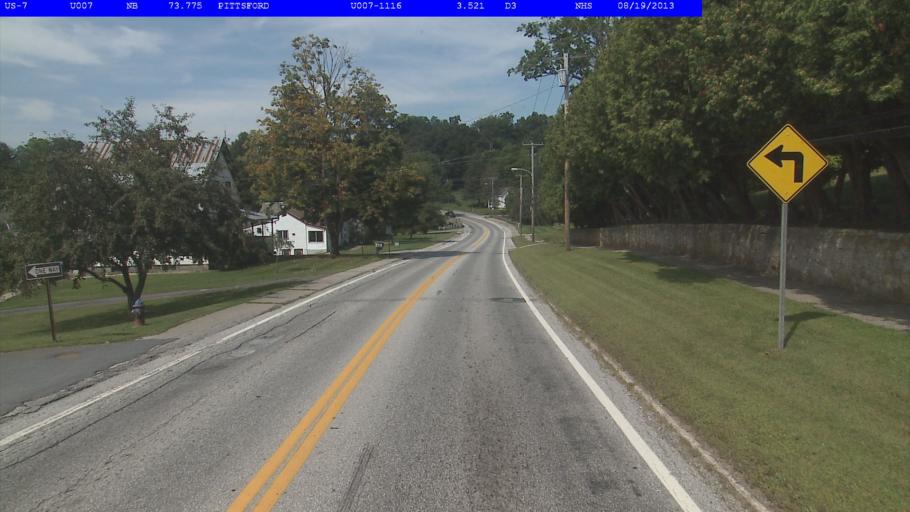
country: US
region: Vermont
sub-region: Rutland County
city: Rutland
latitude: 43.7067
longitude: -73.0192
